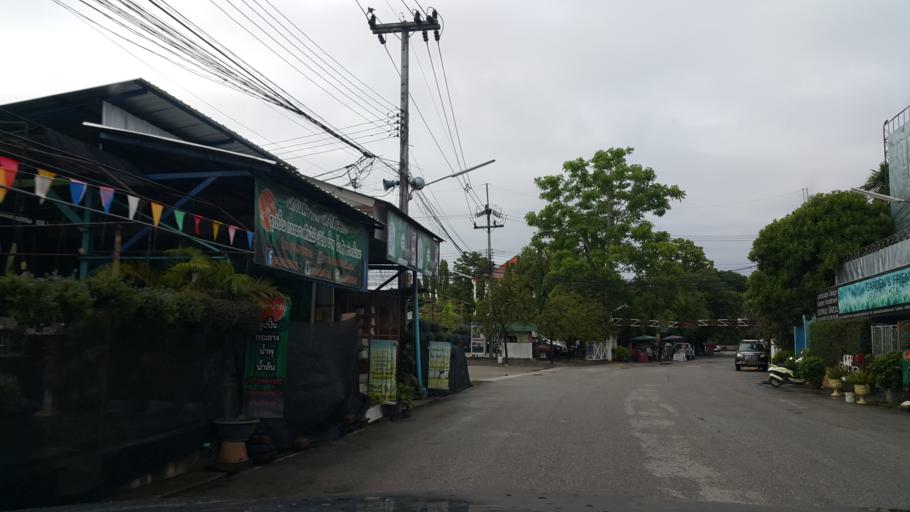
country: TH
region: Chiang Mai
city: Chiang Mai
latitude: 18.8054
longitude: 98.9973
